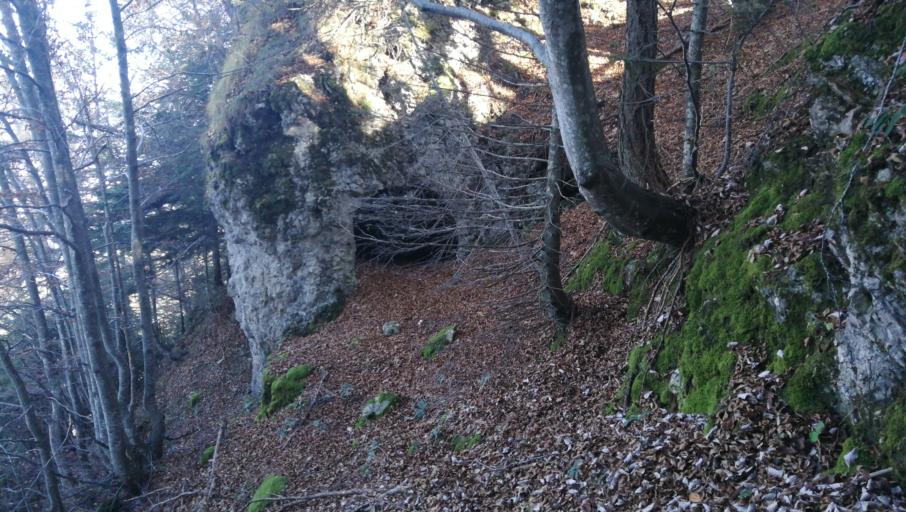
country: IT
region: Trentino-Alto Adige
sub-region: Provincia di Trento
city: Prezzo
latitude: 45.9134
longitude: 10.6493
